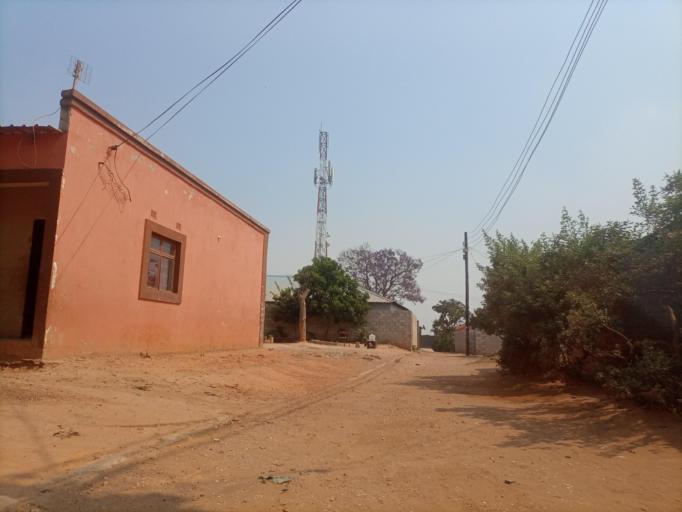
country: ZM
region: Lusaka
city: Lusaka
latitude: -15.4031
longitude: 28.3804
